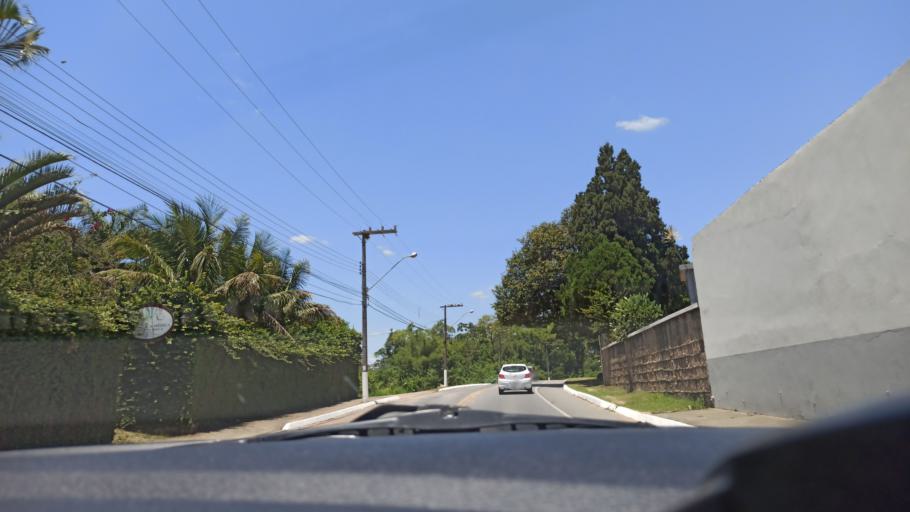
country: BR
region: Santa Catarina
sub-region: Indaial
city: Indaial
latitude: -26.8874
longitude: -49.2396
